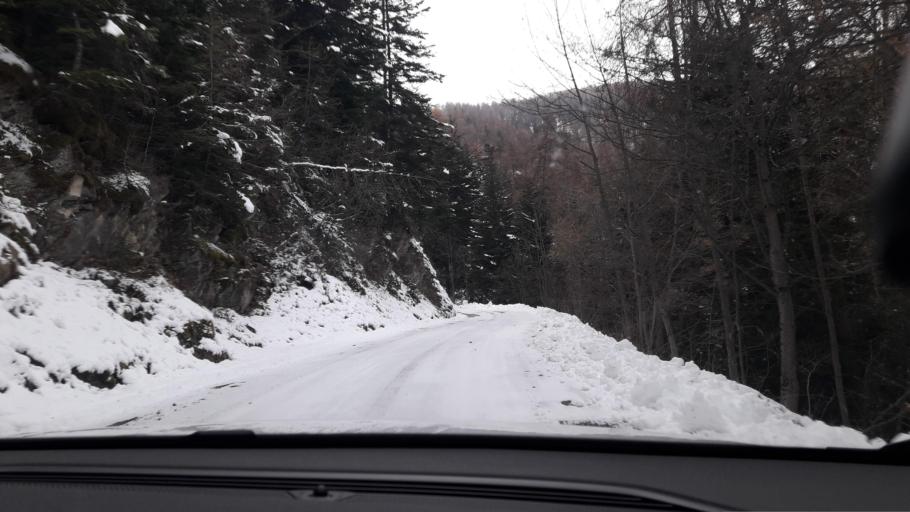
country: FR
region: Rhone-Alpes
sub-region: Departement de la Savoie
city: Valloire
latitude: 45.1979
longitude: 6.4232
